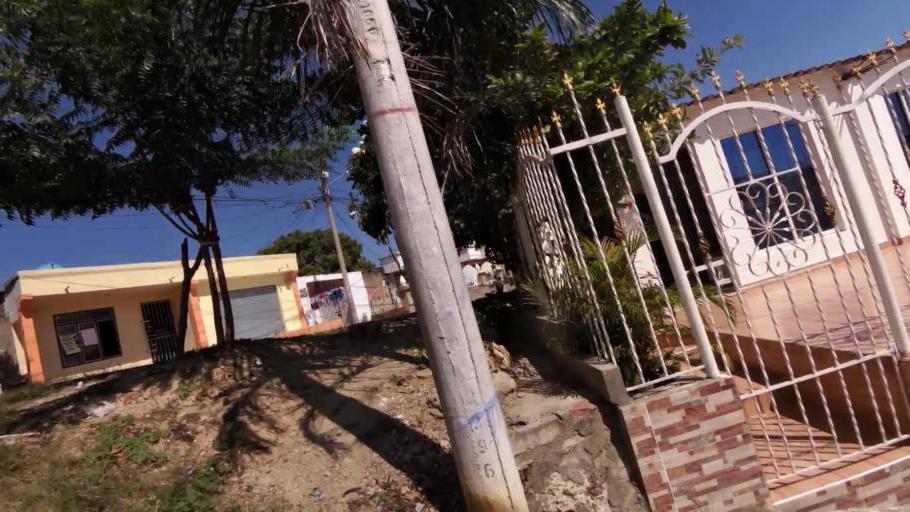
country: CO
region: Bolivar
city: Cartagena
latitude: 10.3919
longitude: -75.5103
